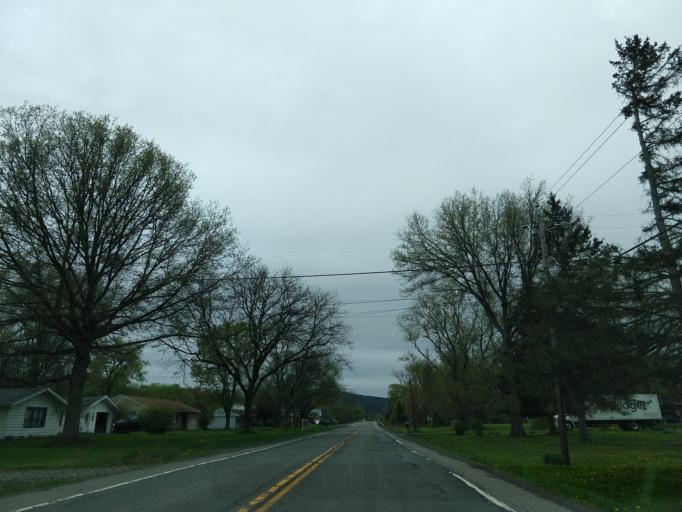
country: US
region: New York
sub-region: Tompkins County
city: Dryden
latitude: 42.5075
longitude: -76.3583
